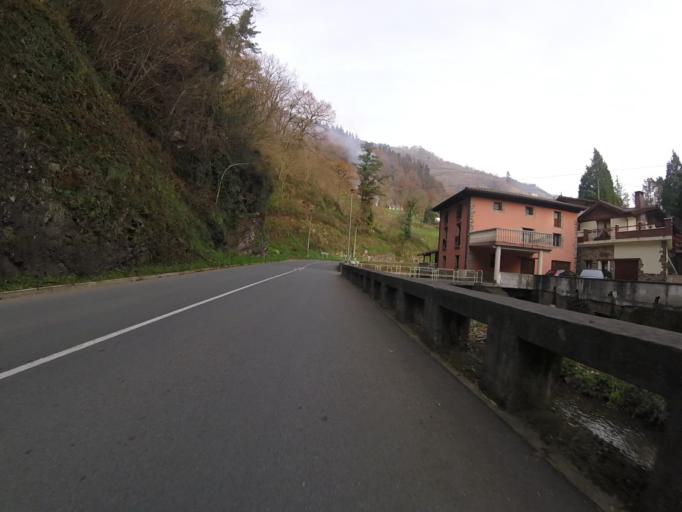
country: ES
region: Basque Country
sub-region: Provincia de Guipuzcoa
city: Berrobi
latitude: 43.1450
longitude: -2.0319
